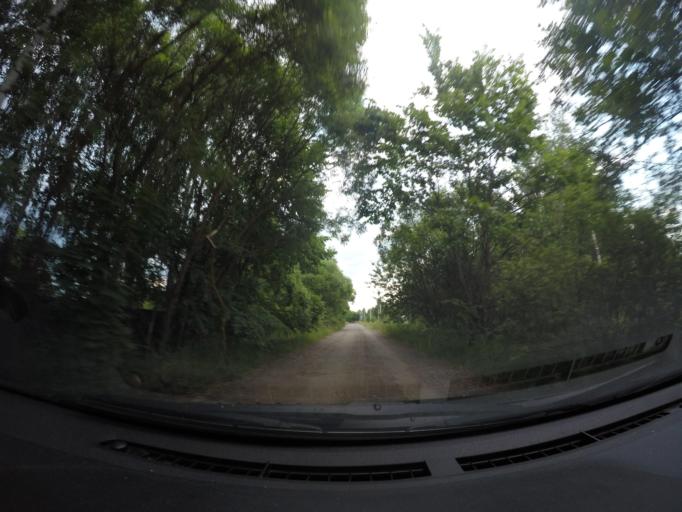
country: RU
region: Moskovskaya
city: Krasnyy Tkach
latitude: 55.4202
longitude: 39.2357
